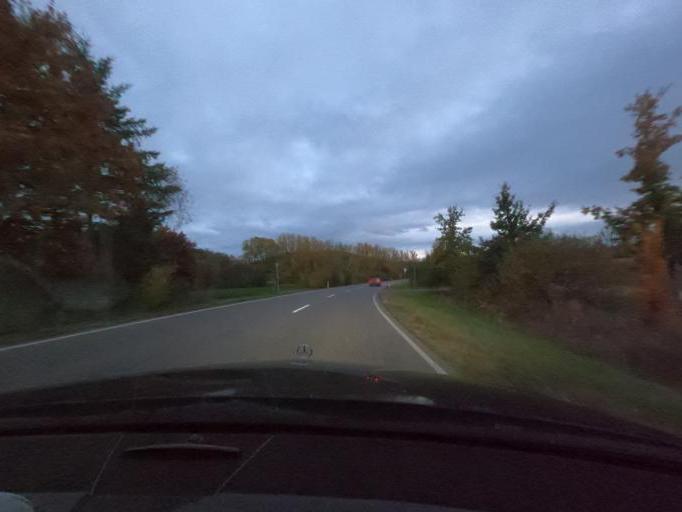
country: DE
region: Thuringia
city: Arenshausen
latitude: 51.3818
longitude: 9.9583
